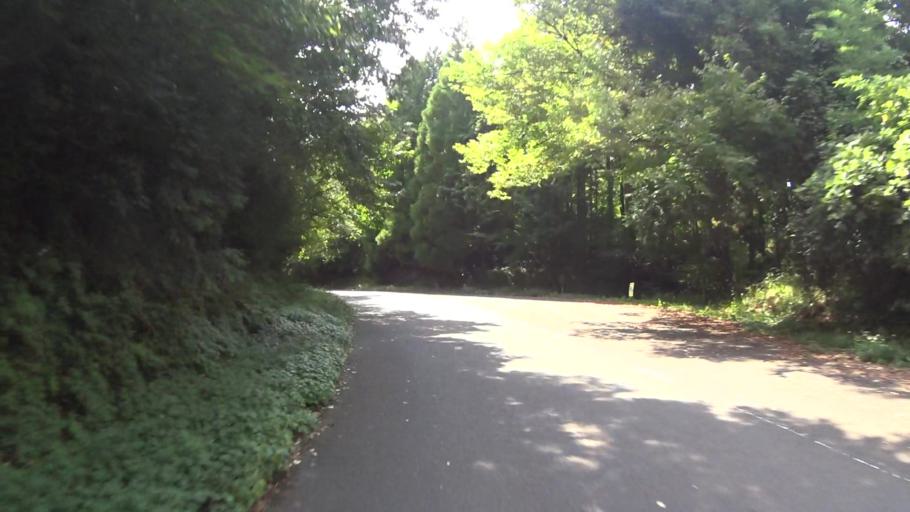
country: JP
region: Kyoto
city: Miyazu
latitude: 35.6571
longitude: 135.1069
